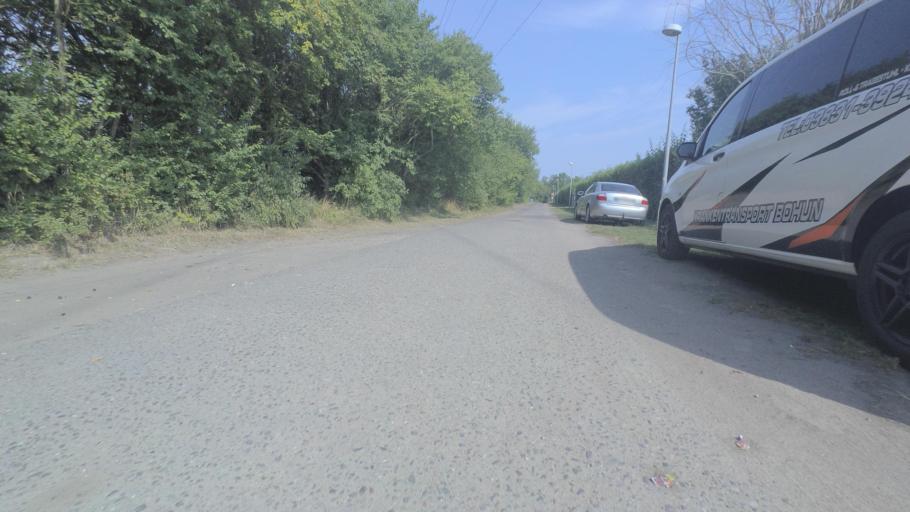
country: DE
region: Mecklenburg-Vorpommern
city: Stralsund
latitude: 54.2822
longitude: 13.0895
